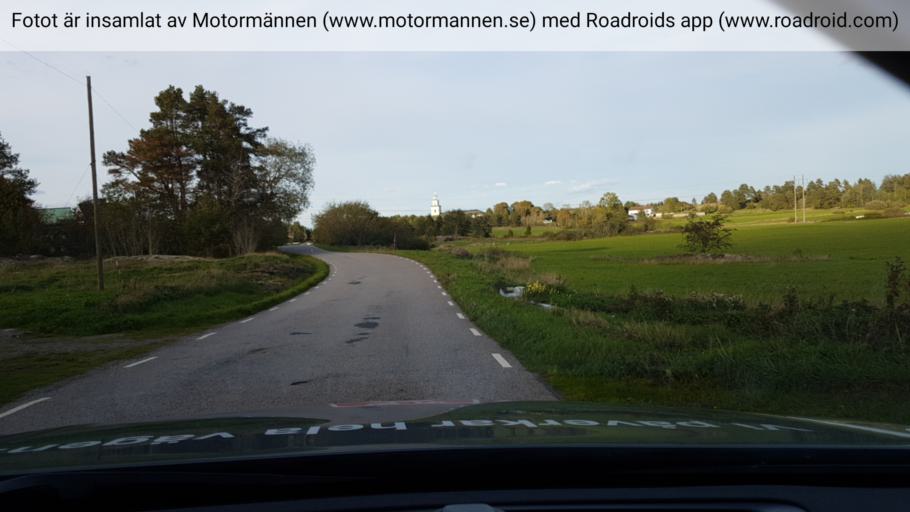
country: SE
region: Kalmar
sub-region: Vasterviks Kommun
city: Forserum
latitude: 57.9306
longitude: 16.4569
